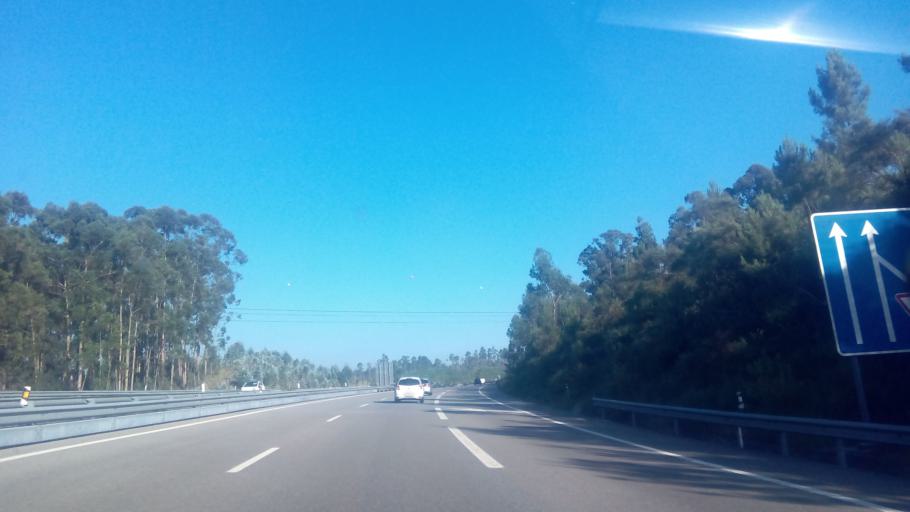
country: PT
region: Porto
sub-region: Pacos de Ferreira
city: Pacos de Ferreira
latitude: 41.2636
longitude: -8.3762
